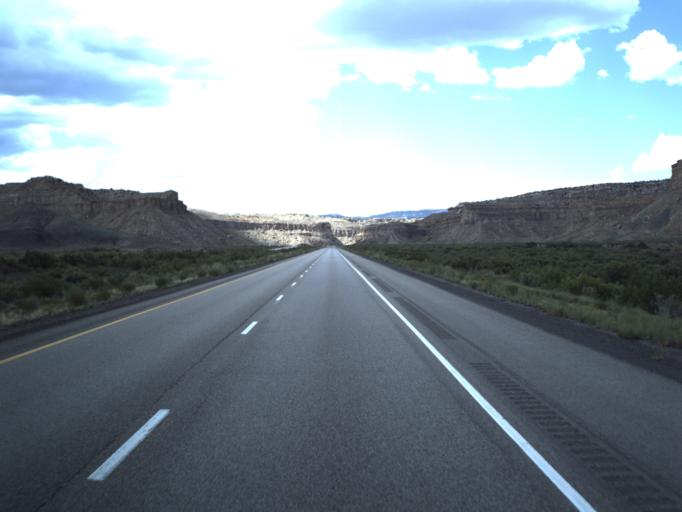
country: US
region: Utah
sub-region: Emery County
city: Ferron
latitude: 38.8099
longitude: -111.2323
